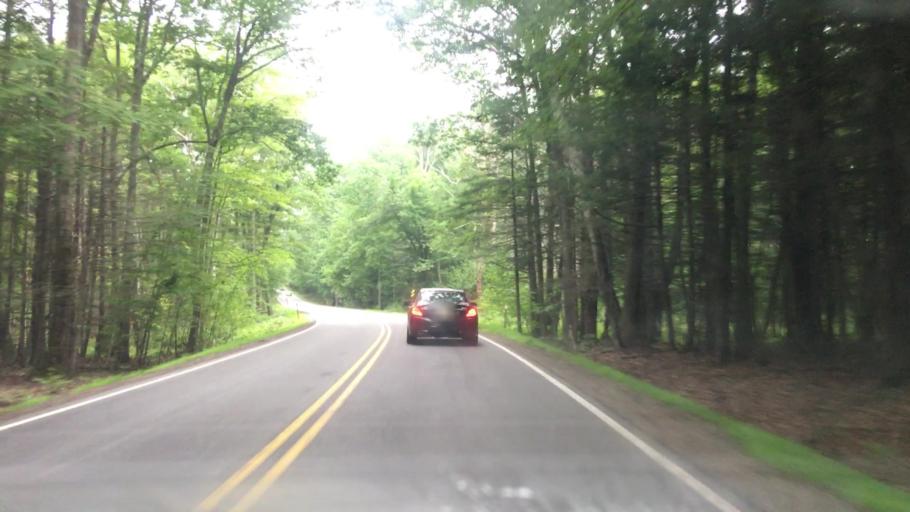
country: US
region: New Hampshire
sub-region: Rockingham County
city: Greenland
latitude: 43.0904
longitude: -70.8376
